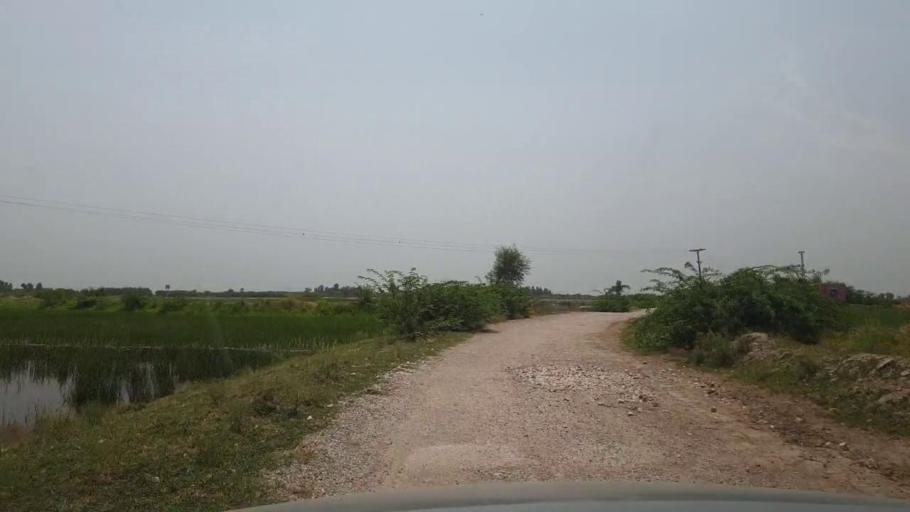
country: PK
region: Sindh
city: Garhi Yasin
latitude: 27.8848
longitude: 68.4954
